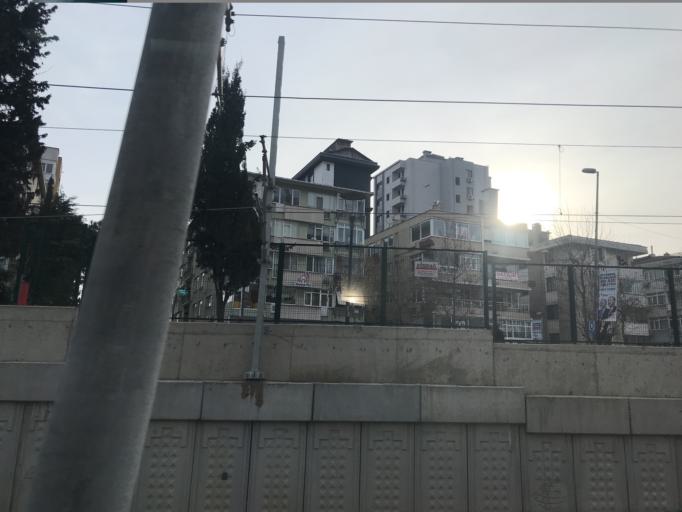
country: TR
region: Istanbul
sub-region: Atasehir
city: Atasehir
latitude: 40.9551
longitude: 29.0917
